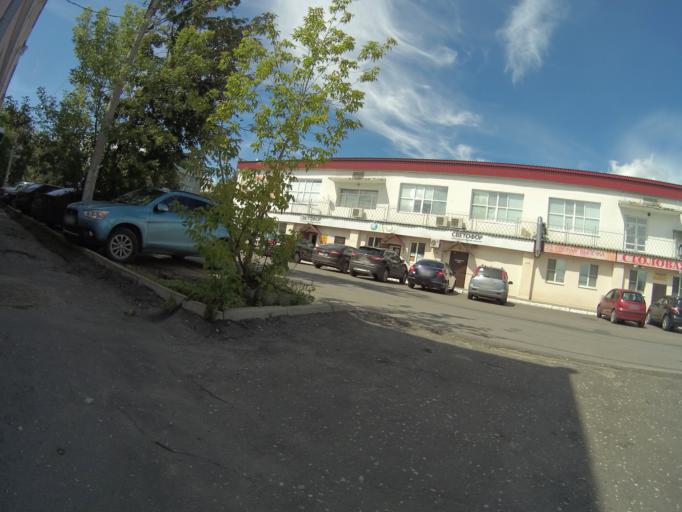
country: RU
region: Vladimir
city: Vladimir
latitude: 56.1379
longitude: 40.4085
